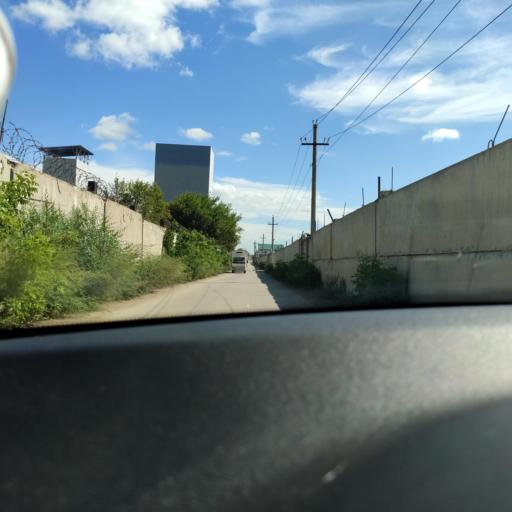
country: RU
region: Samara
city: Samara
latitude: 53.2019
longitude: 50.2691
